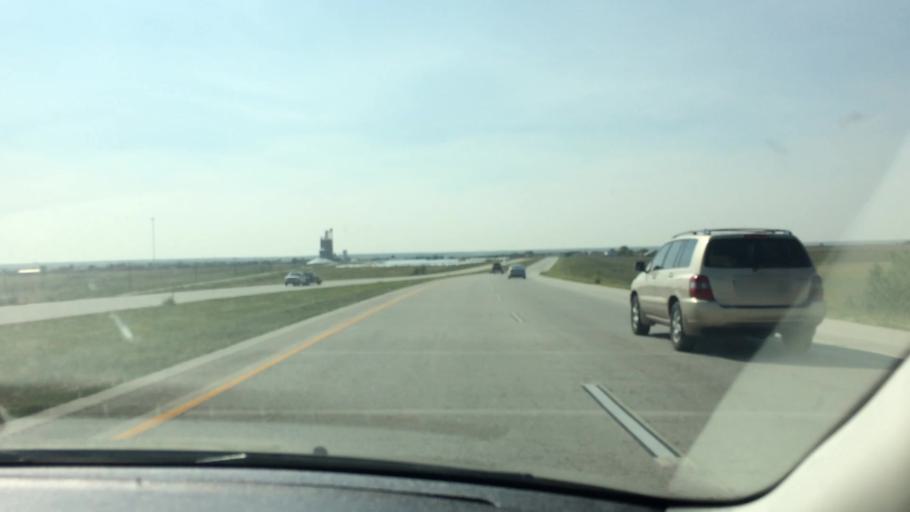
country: US
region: Colorado
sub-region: Arapahoe County
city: Byers
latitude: 39.7053
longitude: -104.1935
